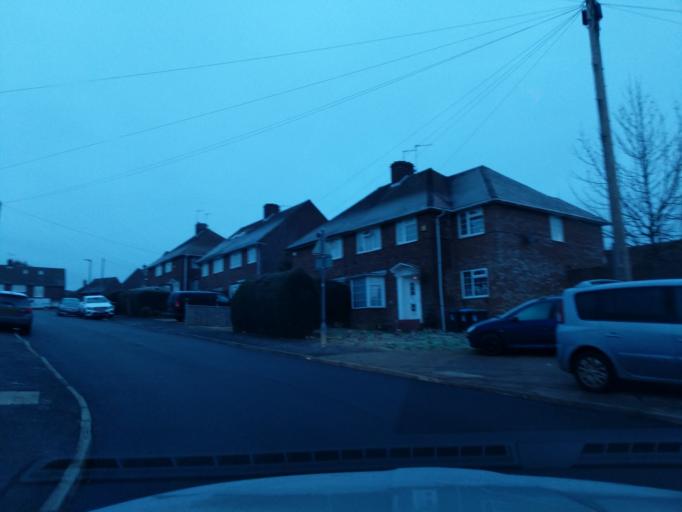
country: GB
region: England
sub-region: Hertfordshire
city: Hemel Hempstead
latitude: 51.7380
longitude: -0.4577
